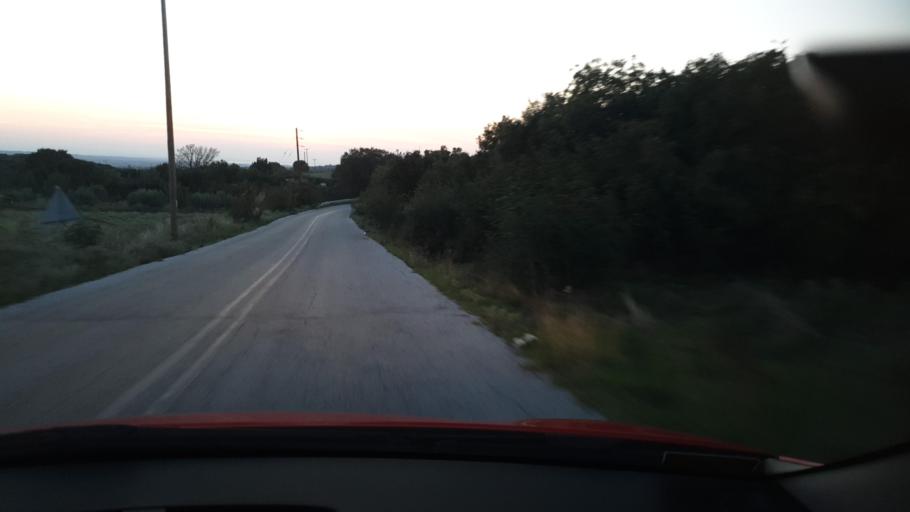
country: GR
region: Central Macedonia
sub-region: Nomos Thessalonikis
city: Vasilika
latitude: 40.5080
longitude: 23.1483
